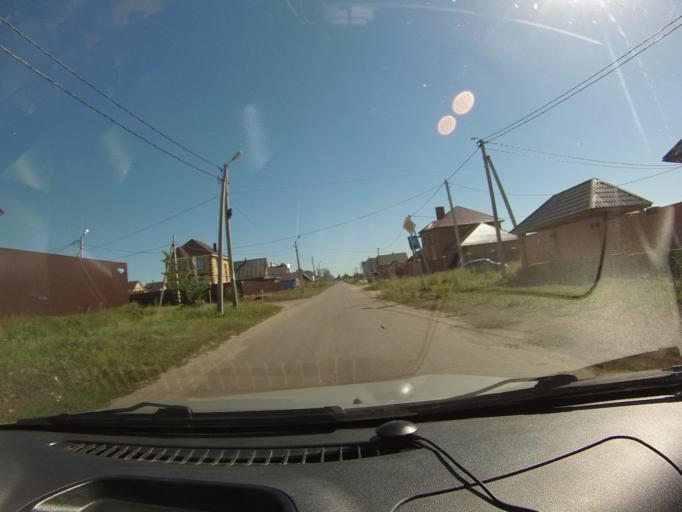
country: RU
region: Tambov
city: Komsomolets
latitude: 52.7720
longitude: 41.3589
